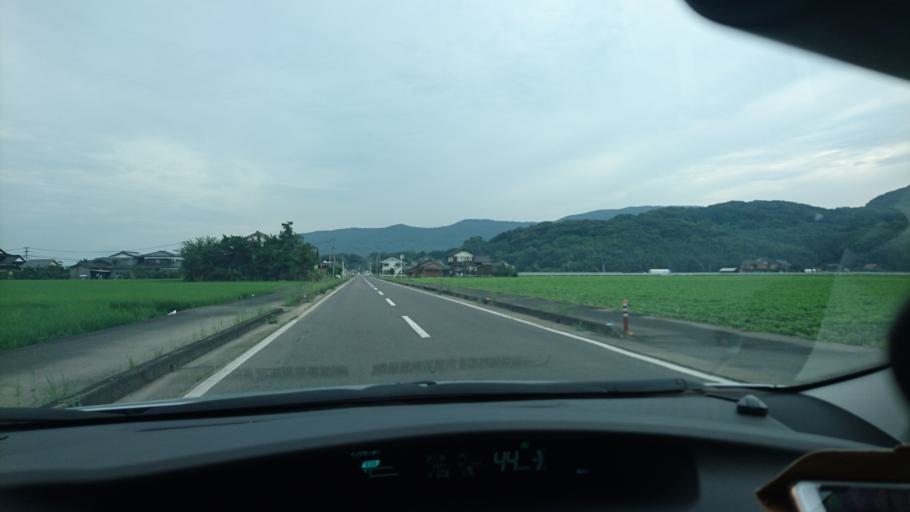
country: JP
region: Saga Prefecture
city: Takeocho-takeo
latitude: 33.1952
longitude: 130.1018
